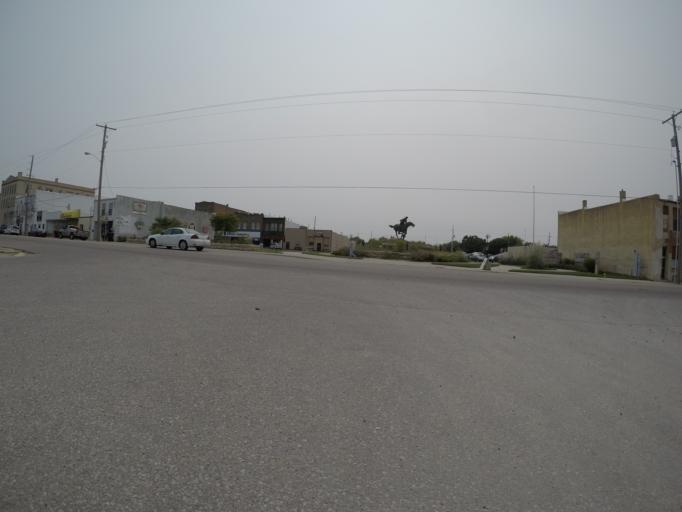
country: US
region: Kansas
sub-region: Marshall County
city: Marysville
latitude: 39.8423
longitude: -96.6493
